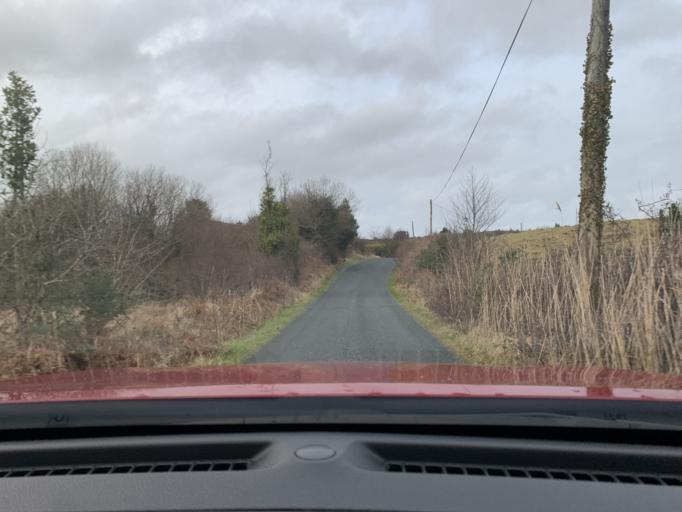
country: IE
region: Connaught
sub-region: Roscommon
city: Boyle
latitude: 53.9761
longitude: -8.4182
